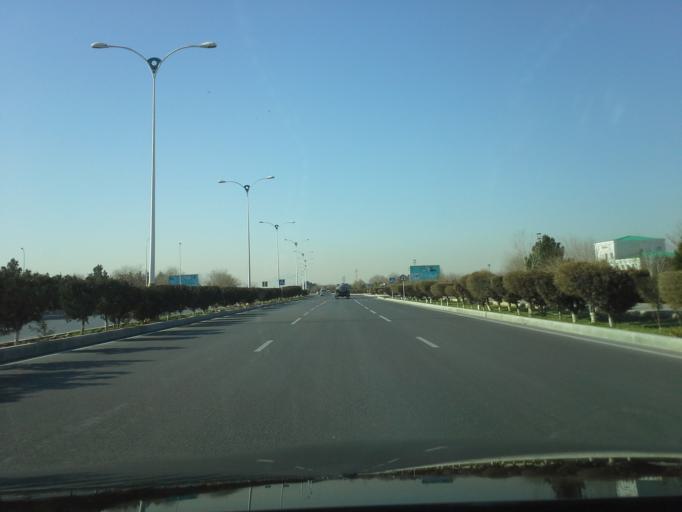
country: TM
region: Ahal
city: Annau
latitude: 37.9104
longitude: 58.5011
